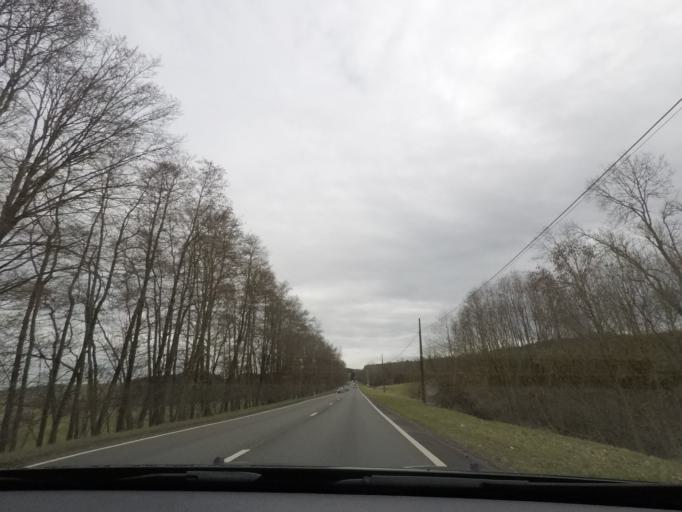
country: BE
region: Wallonia
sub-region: Province du Luxembourg
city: Bastogne
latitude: 49.9792
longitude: 5.7705
